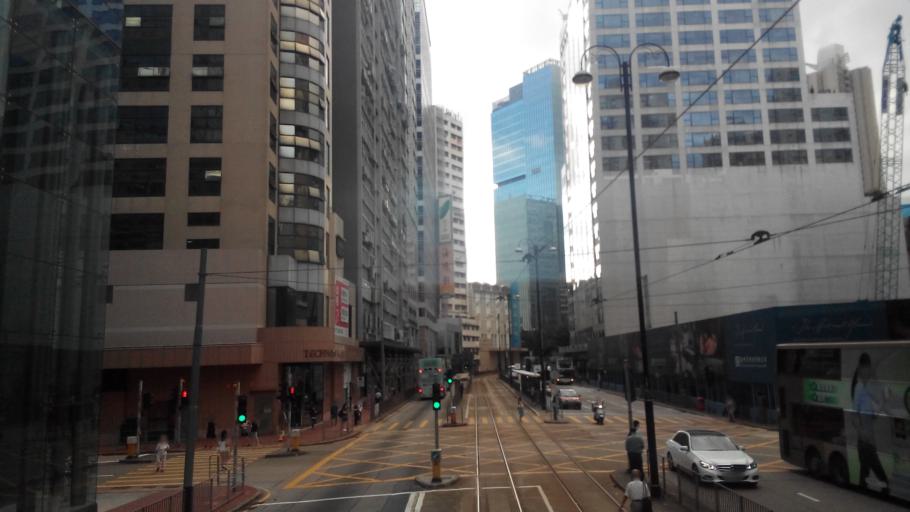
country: HK
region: Kowloon City
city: Kowloon
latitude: 22.2920
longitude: 114.2069
